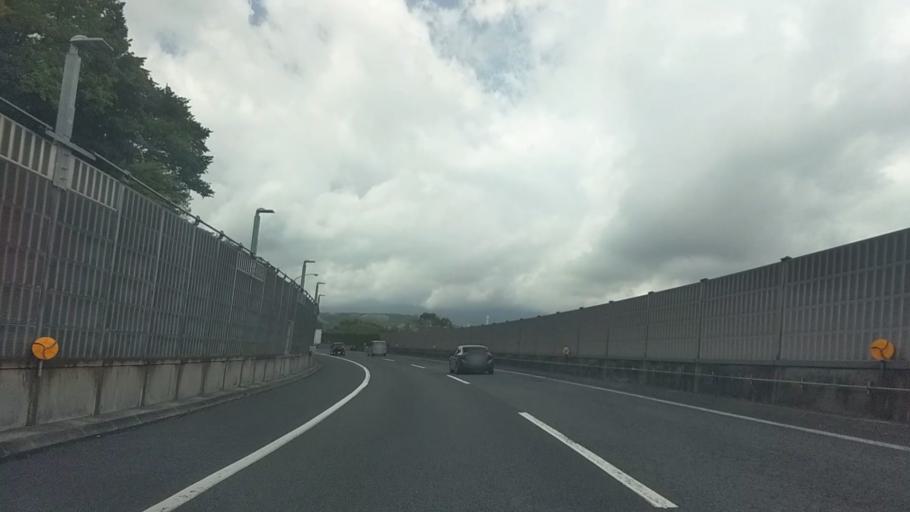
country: JP
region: Shizuoka
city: Gotemba
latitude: 35.3574
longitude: 139.0009
